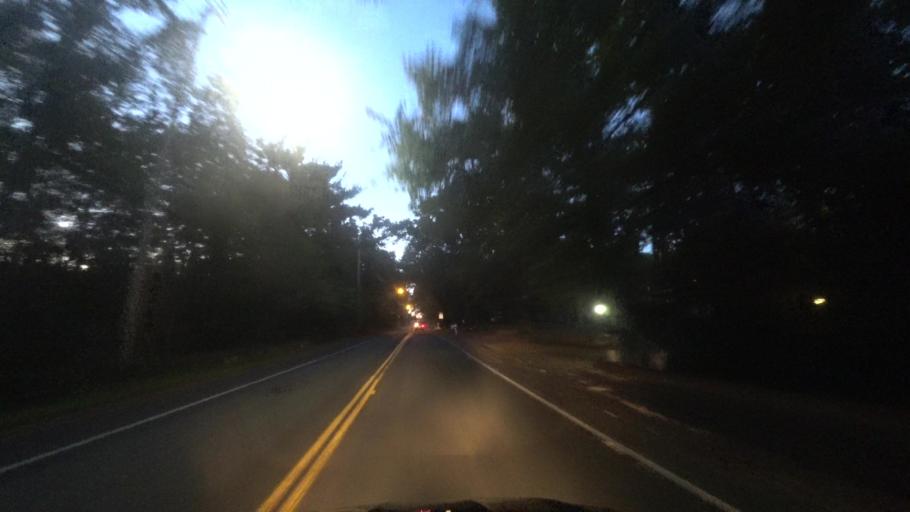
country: US
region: Massachusetts
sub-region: Middlesex County
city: Reading
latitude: 42.5304
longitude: -71.0820
